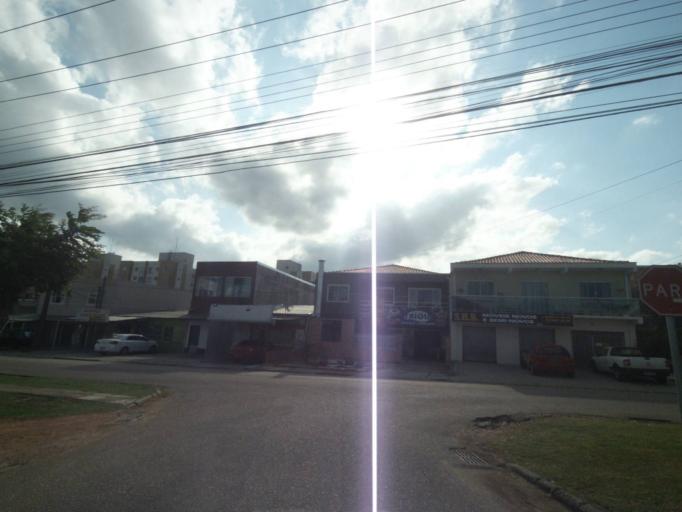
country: BR
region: Parana
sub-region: Curitiba
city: Curitiba
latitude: -25.4964
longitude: -49.3234
